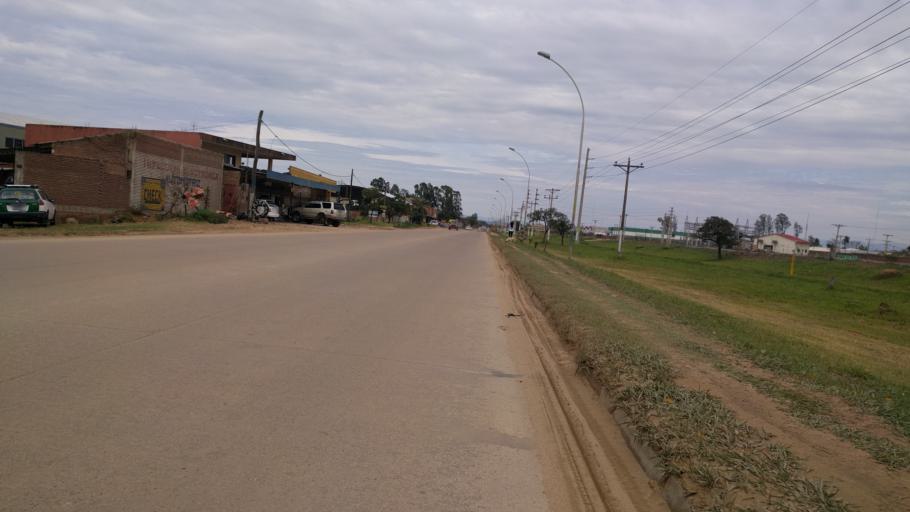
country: BO
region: Santa Cruz
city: Santa Cruz de la Sierra
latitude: -17.8469
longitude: -63.1765
